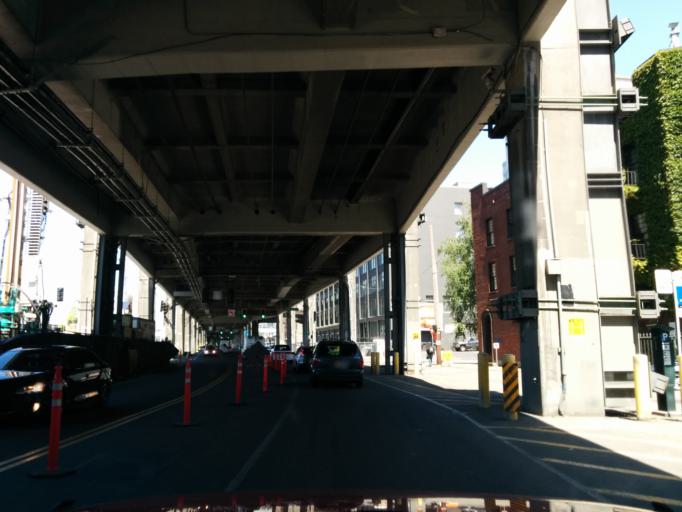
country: US
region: Washington
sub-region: King County
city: Seattle
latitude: 47.6012
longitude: -122.3357
